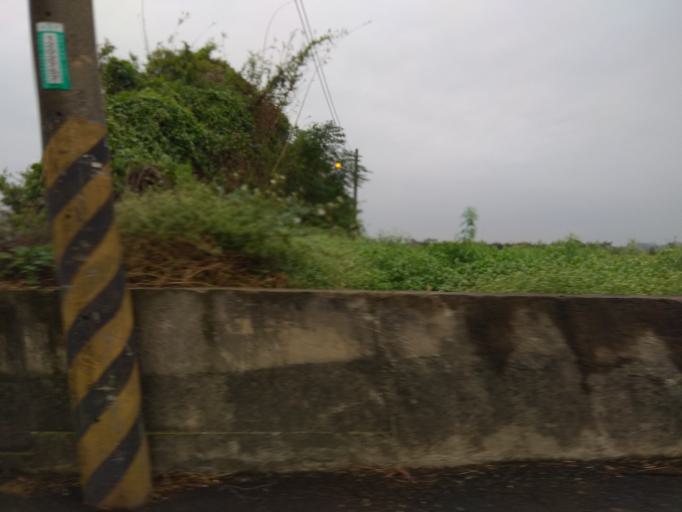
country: TW
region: Taiwan
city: Taoyuan City
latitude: 25.0337
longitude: 121.2239
